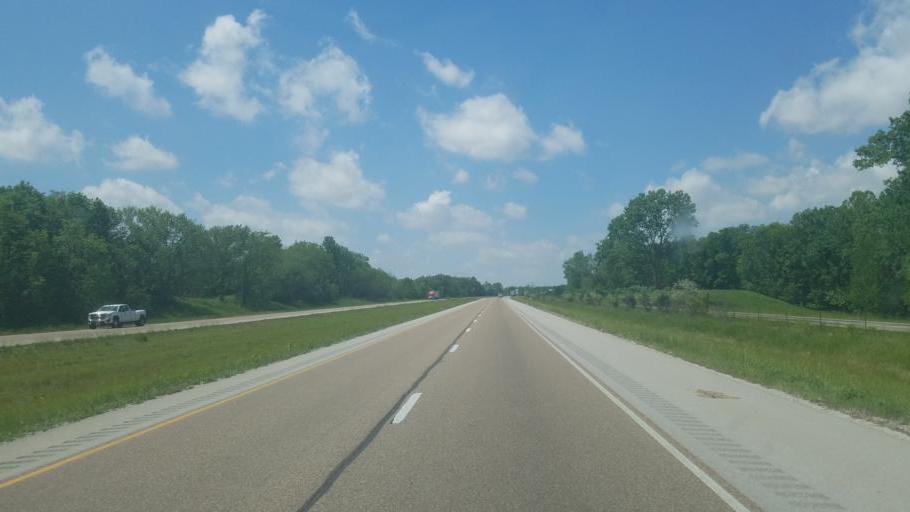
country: US
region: Illinois
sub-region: Cumberland County
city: Greenup
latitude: 39.2654
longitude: -88.1218
